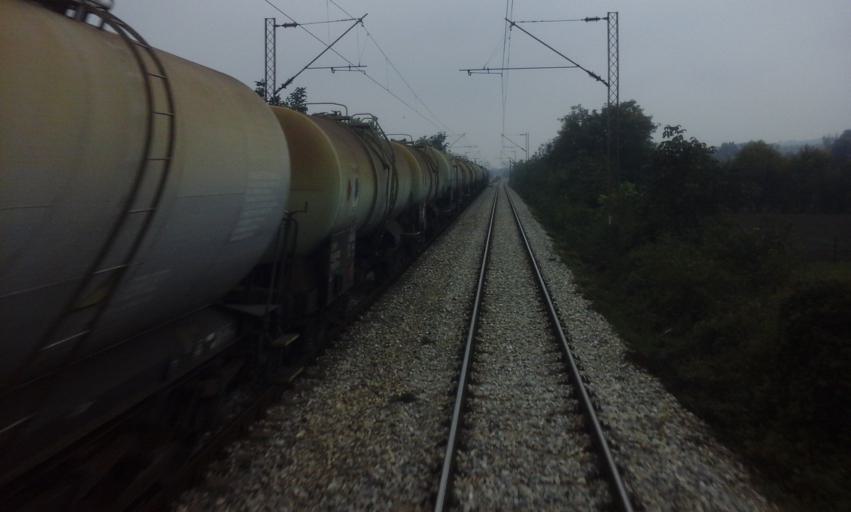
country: RS
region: Central Serbia
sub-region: Sumadijski Okrug
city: Lapovo
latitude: 44.2272
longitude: 21.0955
